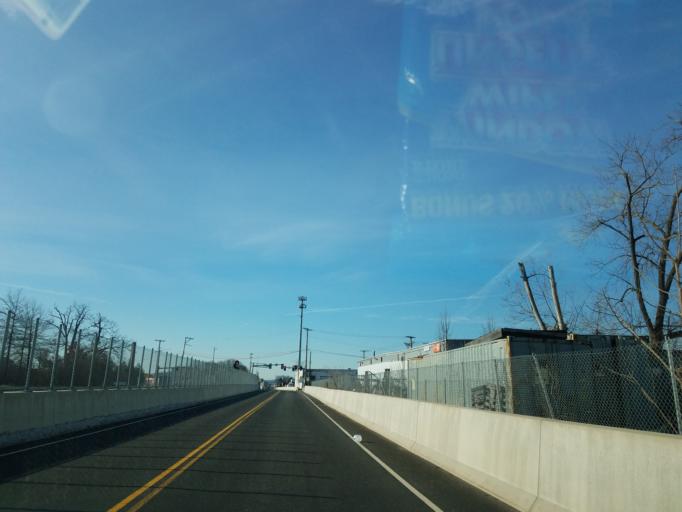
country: US
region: Connecticut
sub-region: Hartford County
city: West Hartford
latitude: 41.7382
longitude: -72.7188
